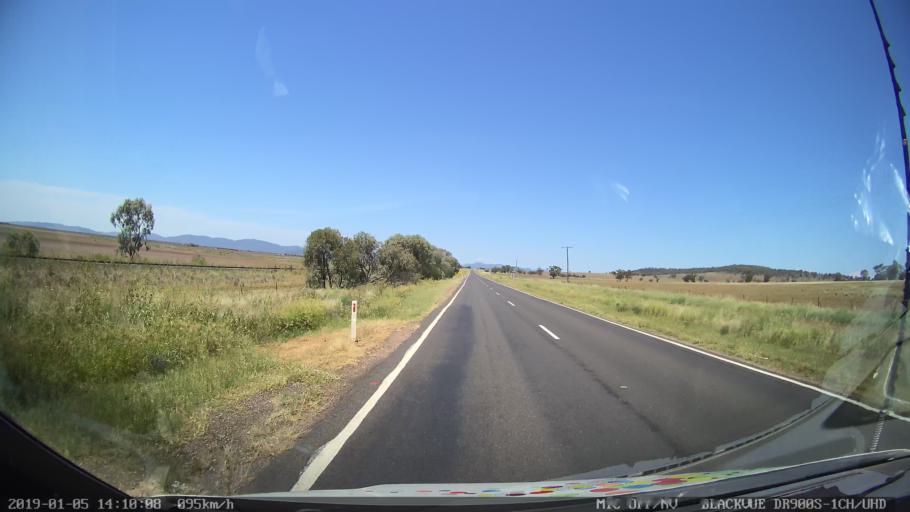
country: AU
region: New South Wales
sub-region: Gunnedah
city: Gunnedah
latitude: -31.2466
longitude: 150.4372
